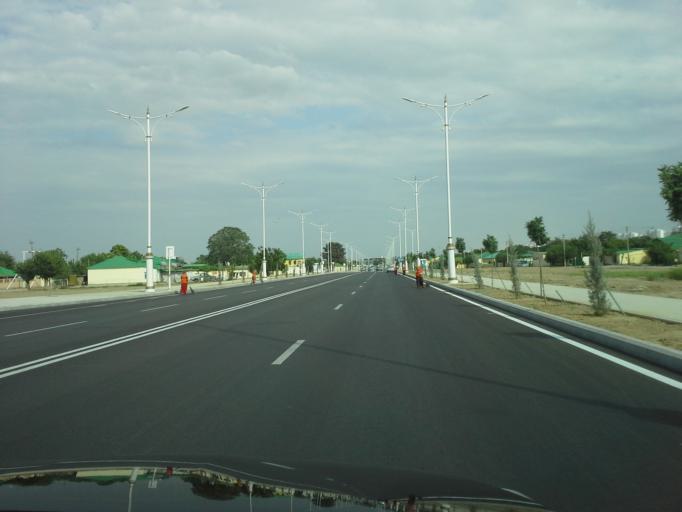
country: TM
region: Ahal
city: Ashgabat
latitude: 37.9631
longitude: 58.3318
